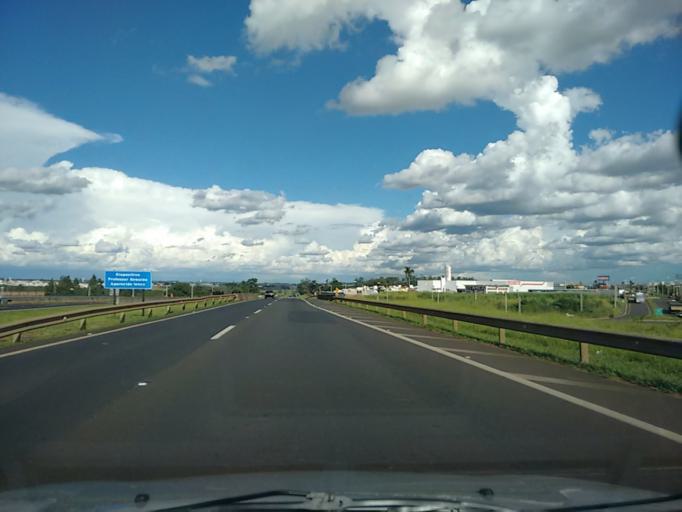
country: BR
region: Sao Paulo
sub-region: Sao Carlos
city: Sao Carlos
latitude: -21.9763
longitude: -47.9333
